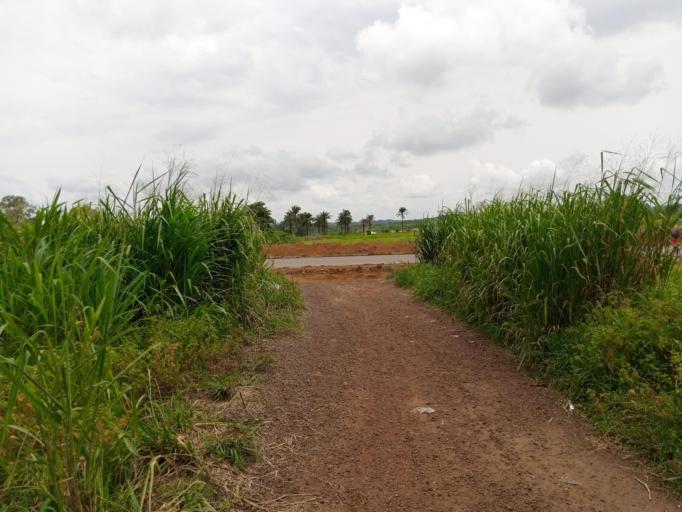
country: SL
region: Southern Province
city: Moyamba
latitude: 8.1657
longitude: -12.4227
